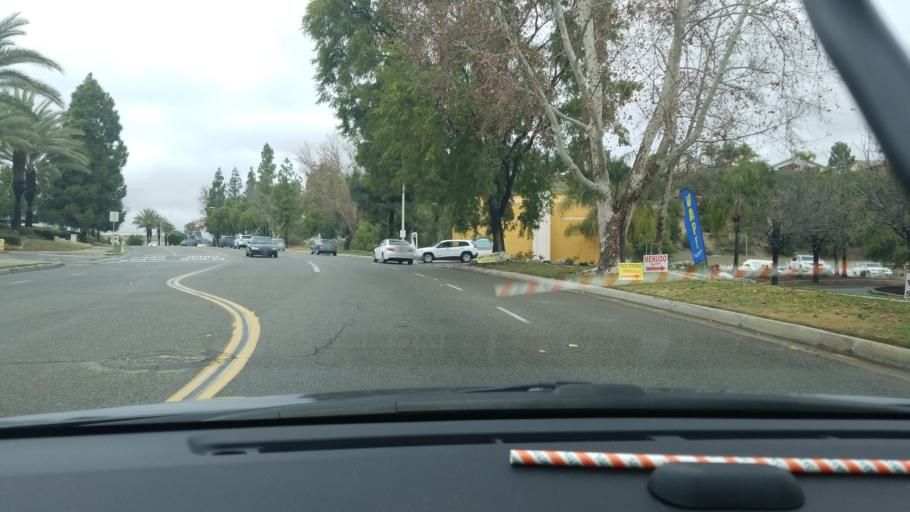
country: US
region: California
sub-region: Riverside County
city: Murrieta Hot Springs
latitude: 33.5569
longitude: -117.1775
